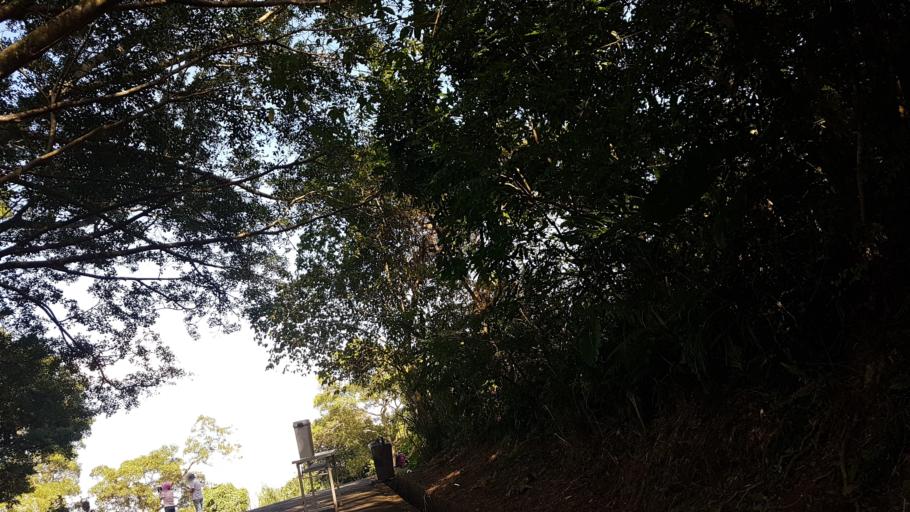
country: TW
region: Taipei
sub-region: Taipei
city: Banqiao
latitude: 24.9491
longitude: 121.5321
